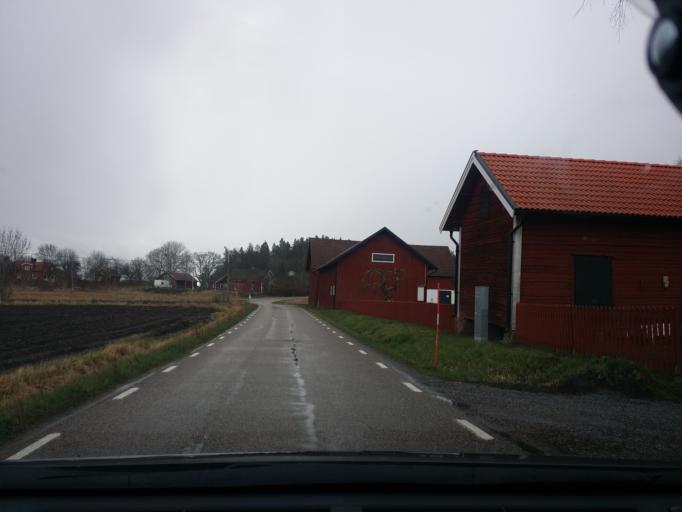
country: SE
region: Uppsala
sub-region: Enkopings Kommun
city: Enkoping
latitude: 59.6577
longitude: 17.0412
